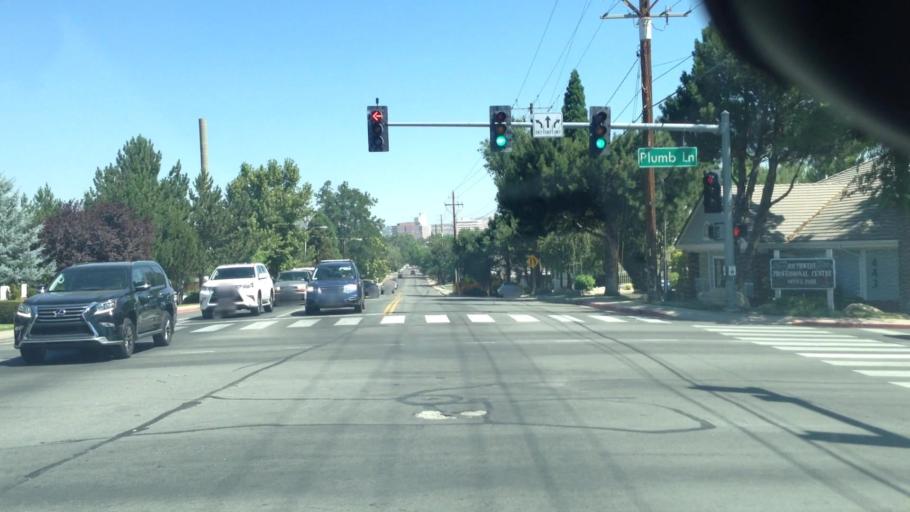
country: US
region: Nevada
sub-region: Washoe County
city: Reno
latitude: 39.5056
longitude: -119.8126
